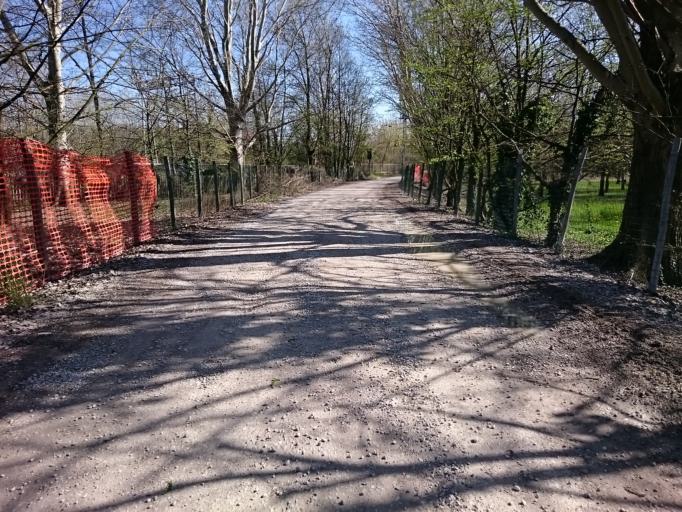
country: IT
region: Veneto
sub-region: Provincia di Padova
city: Noventa
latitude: 45.4013
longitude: 11.9234
